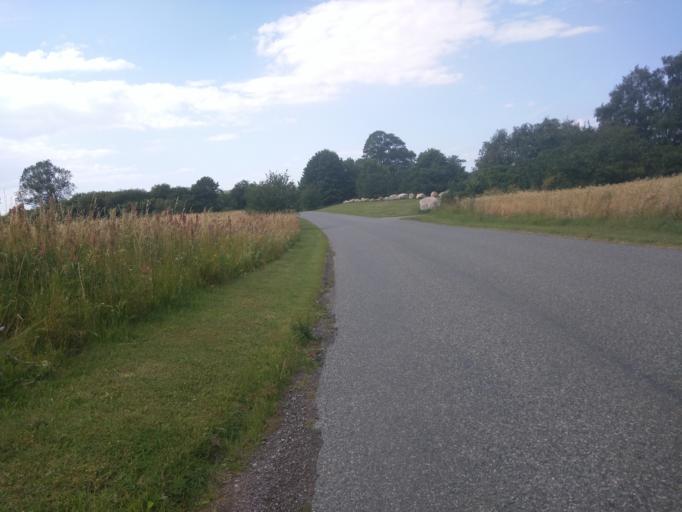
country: DK
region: Zealand
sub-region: Kalundborg Kommune
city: Svebolle
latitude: 55.6885
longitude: 11.2917
